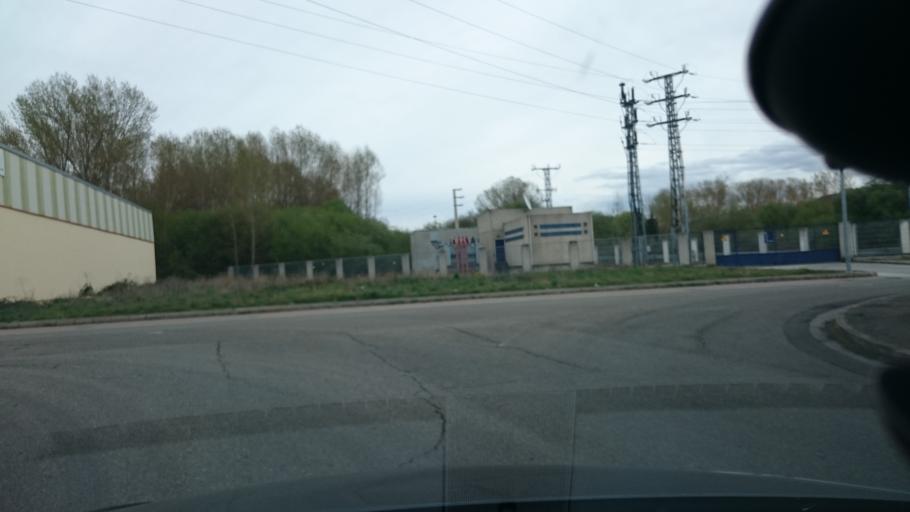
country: ES
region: Castille and Leon
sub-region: Provincia de Leon
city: Camponaraya
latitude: 42.5644
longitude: -6.6546
